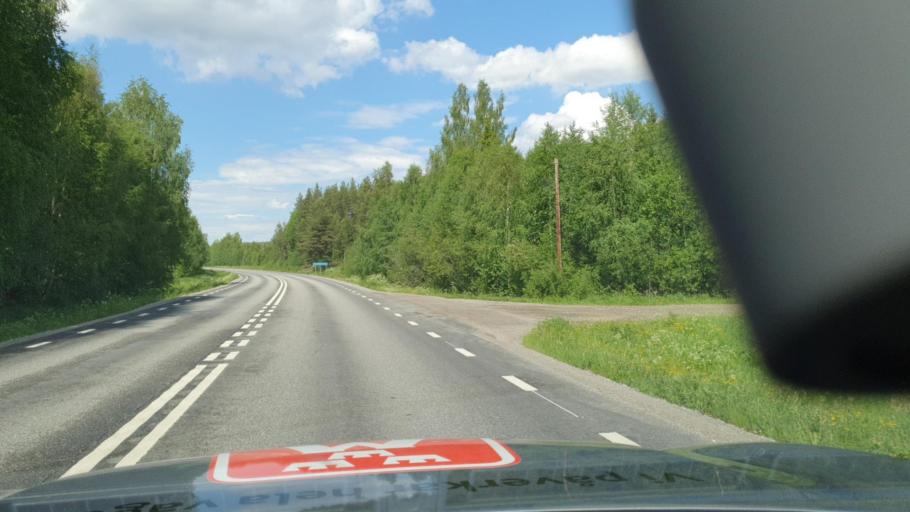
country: SE
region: Vaesternorrland
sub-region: Solleftea Kommun
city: As
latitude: 63.4991
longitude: 16.8647
